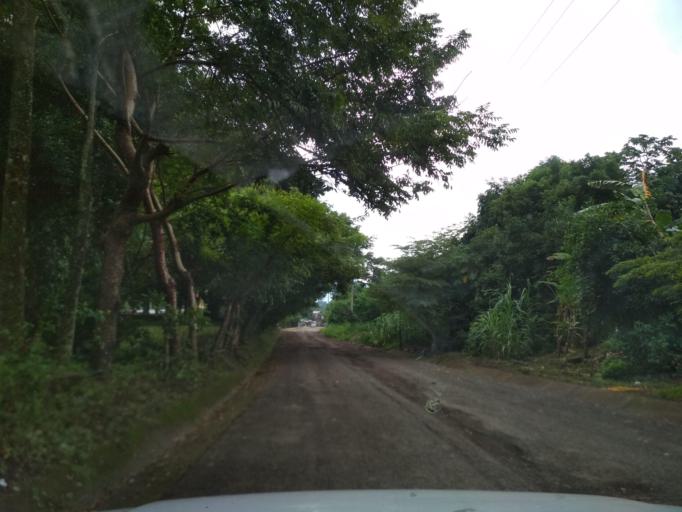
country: MX
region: Veracruz
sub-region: San Andres Tuxtla
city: Matacapan
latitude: 18.4429
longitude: -95.1787
